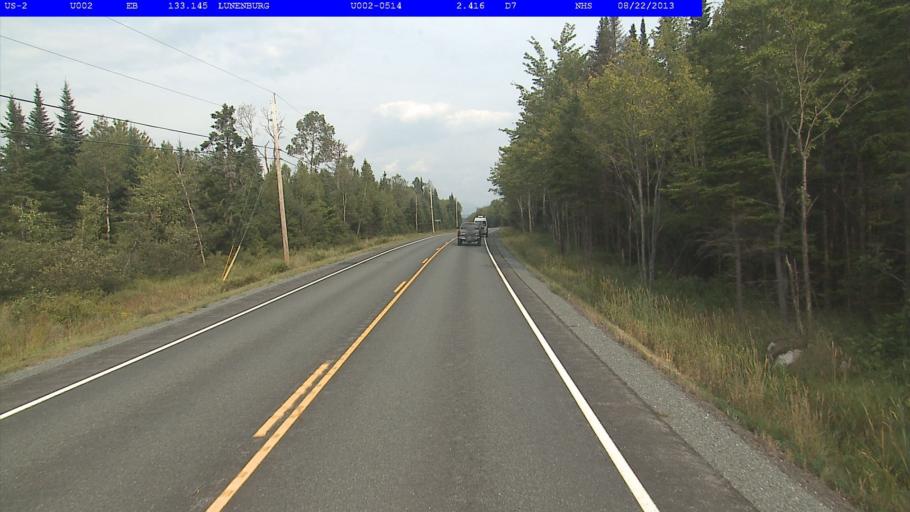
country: US
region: New Hampshire
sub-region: Coos County
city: Whitefield
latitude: 44.4646
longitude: -71.7274
